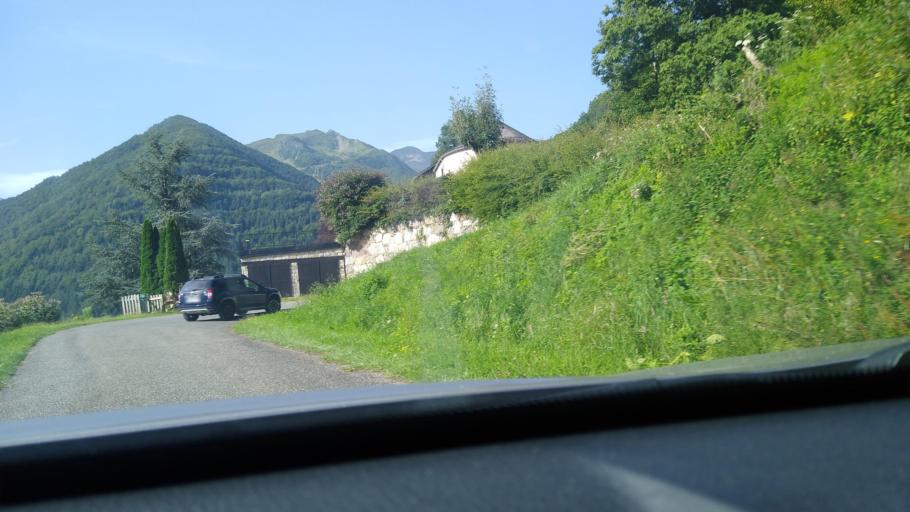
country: FR
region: Midi-Pyrenees
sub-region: Departement de l'Ariege
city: Saint-Girons
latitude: 42.7945
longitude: 1.1855
